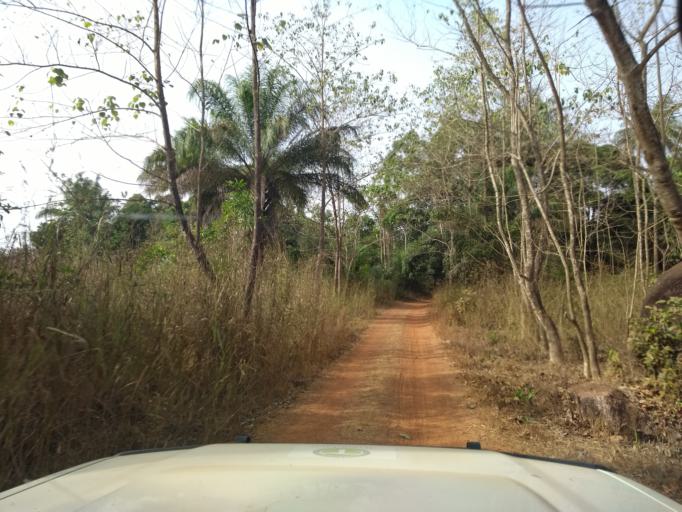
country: GN
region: Kindia
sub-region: Prefecture de Dubreka
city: Dubreka
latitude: 9.8414
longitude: -13.5609
